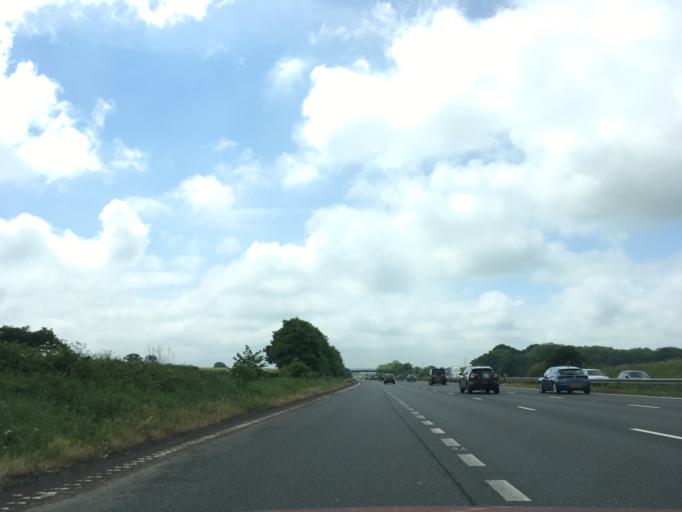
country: GB
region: England
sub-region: Devon
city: Uffculme
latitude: 50.9138
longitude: -3.3605
